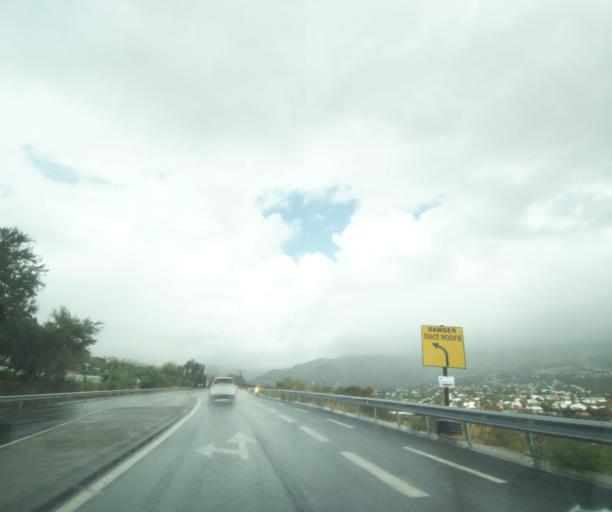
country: RE
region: Reunion
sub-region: Reunion
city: Le Port
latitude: -20.9735
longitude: 55.3163
